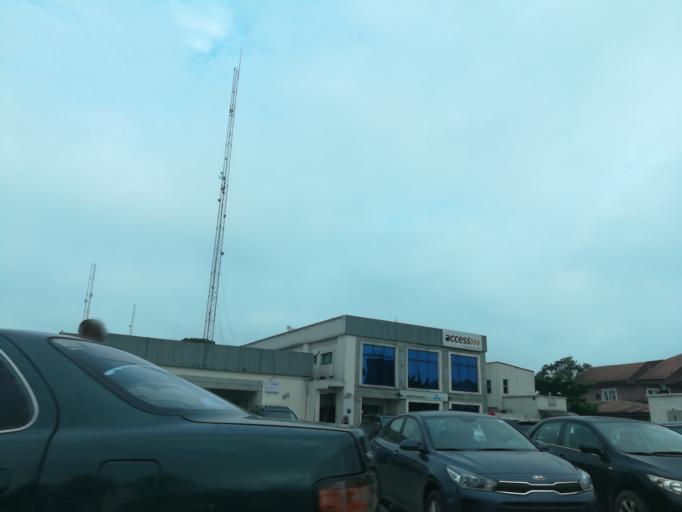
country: NG
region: Rivers
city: Port Harcourt
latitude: 4.8157
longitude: 7.0053
